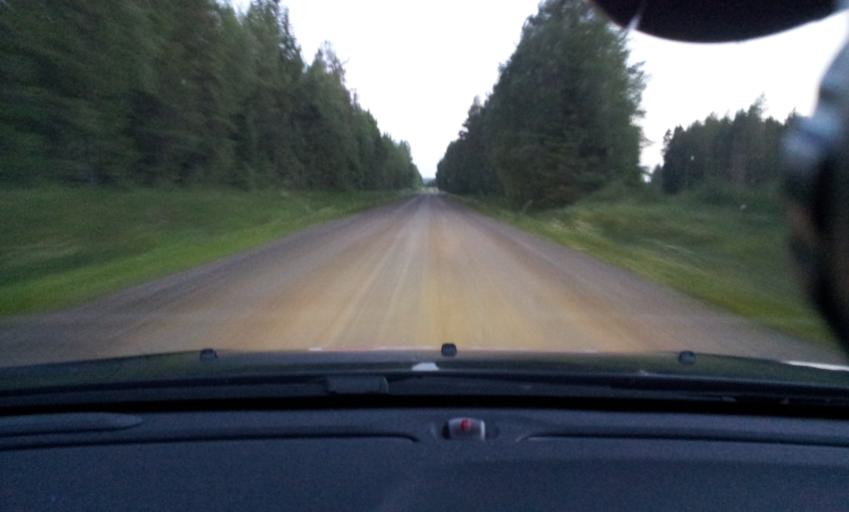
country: SE
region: Vaesternorrland
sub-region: Ange Kommun
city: Ange
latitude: 62.7565
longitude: 15.6619
